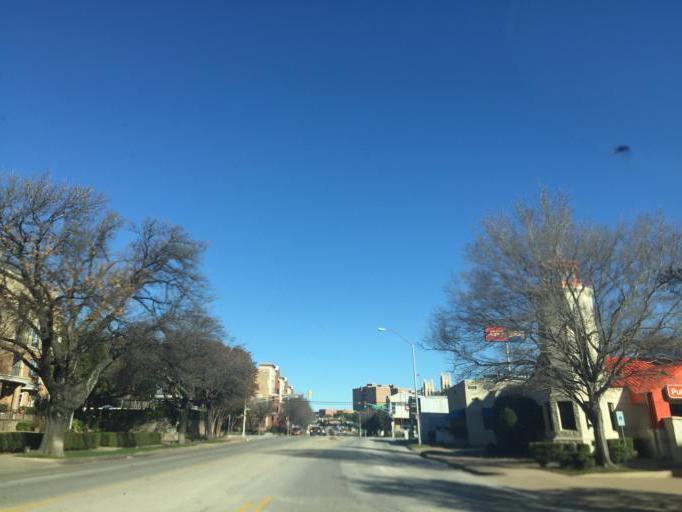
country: US
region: Texas
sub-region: Tarrant County
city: Fort Worth
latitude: 32.7480
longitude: -97.3374
